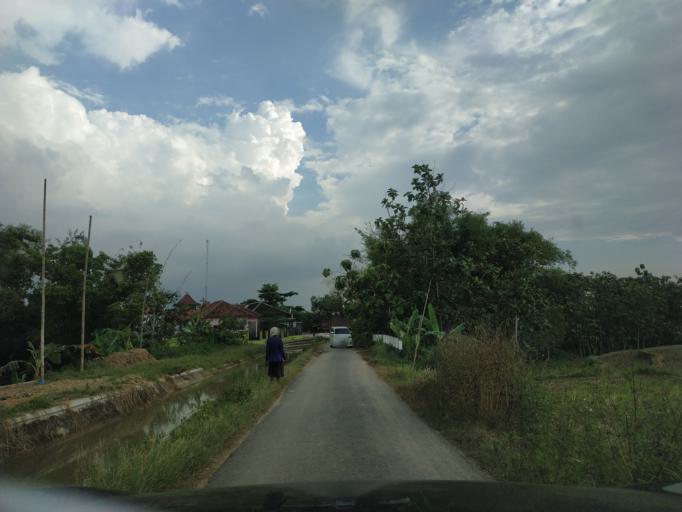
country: ID
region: Central Java
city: Tempuran
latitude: -6.9102
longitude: 111.4601
